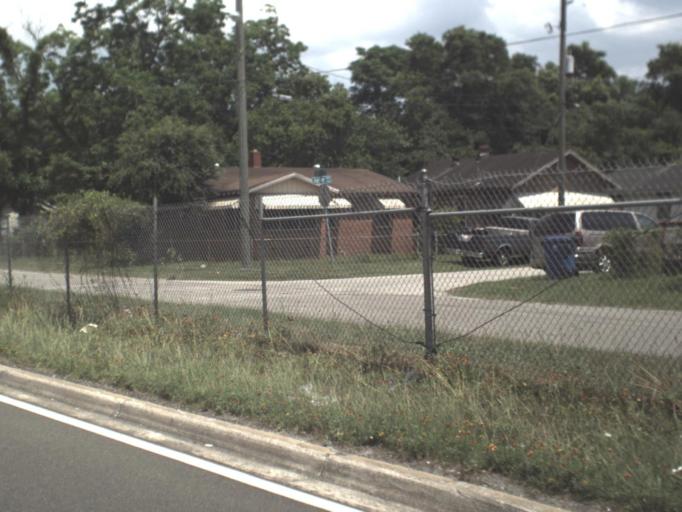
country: US
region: Florida
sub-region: Duval County
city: Jacksonville
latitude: 30.3560
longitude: -81.6651
